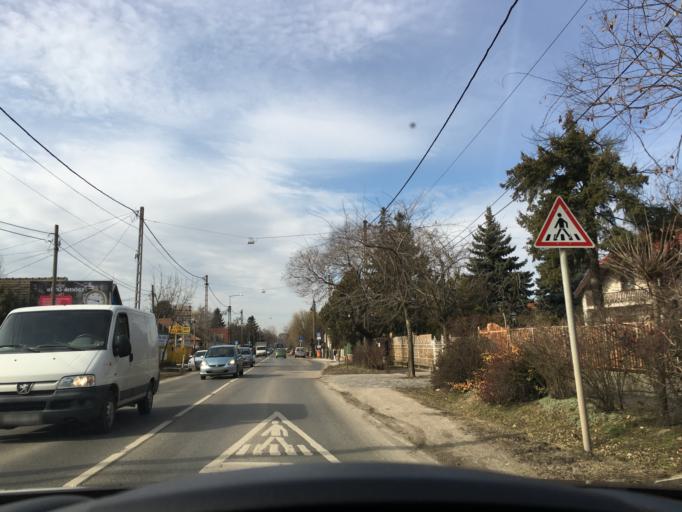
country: HU
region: Budapest
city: Budapest XVII. keruelet
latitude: 47.4857
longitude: 19.2831
